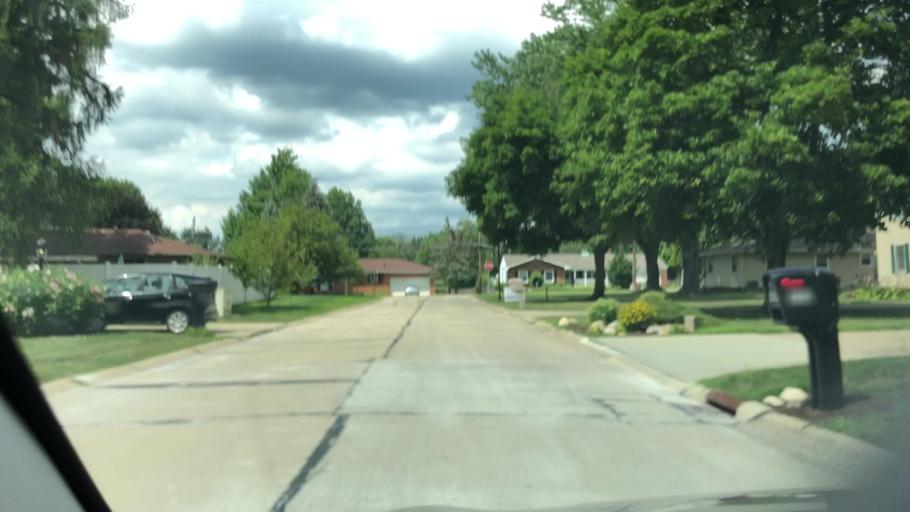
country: US
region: Ohio
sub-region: Summit County
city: Fairlawn
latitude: 41.1254
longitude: -81.6332
